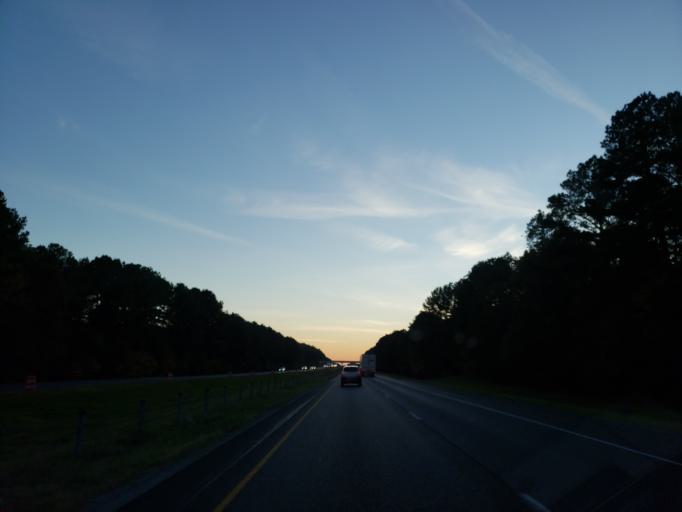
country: US
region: Alabama
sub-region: Sumter County
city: Livingston
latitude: 32.5601
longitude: -88.2606
